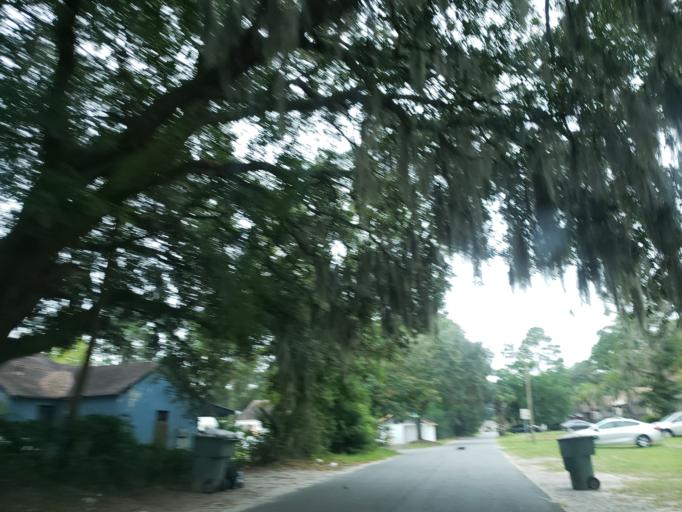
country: US
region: Georgia
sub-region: Chatham County
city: Thunderbolt
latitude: 32.0486
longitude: -81.0725
